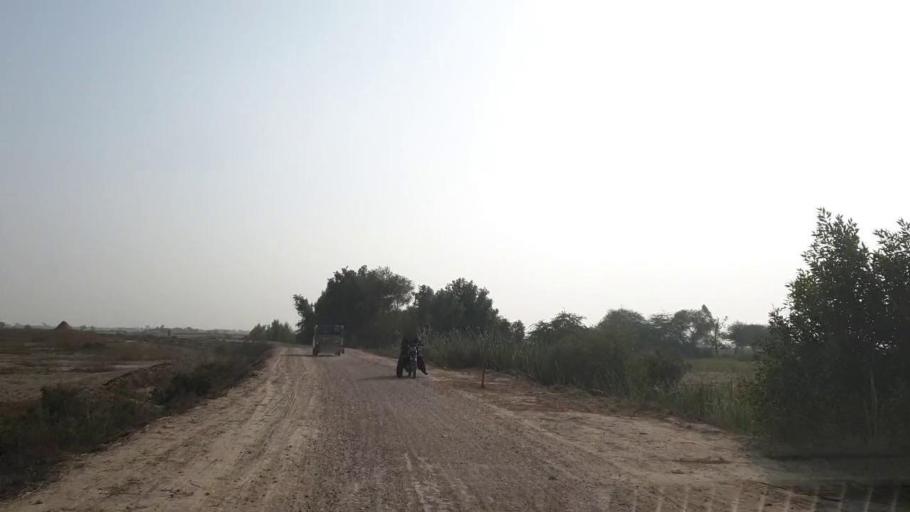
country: PK
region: Sindh
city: Kario
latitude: 24.9152
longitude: 68.5688
